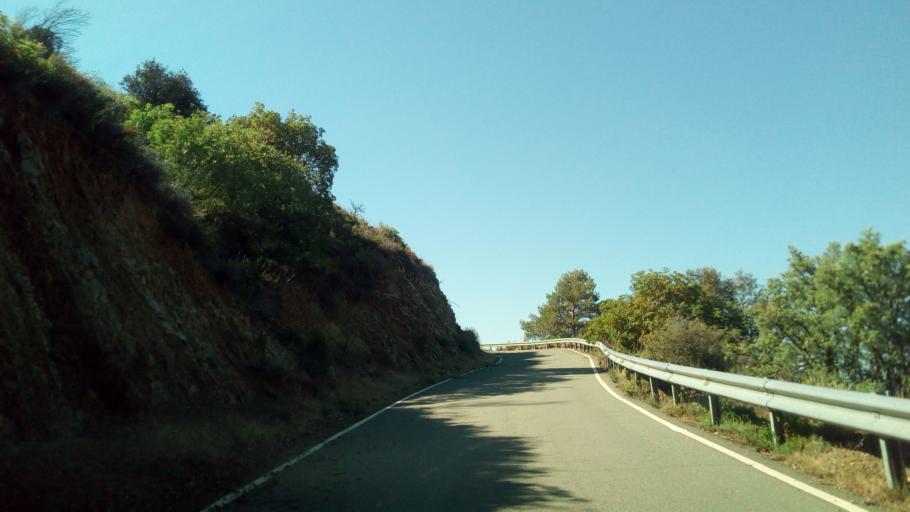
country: CY
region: Lefkosia
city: Lythrodontas
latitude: 34.8837
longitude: 33.2020
